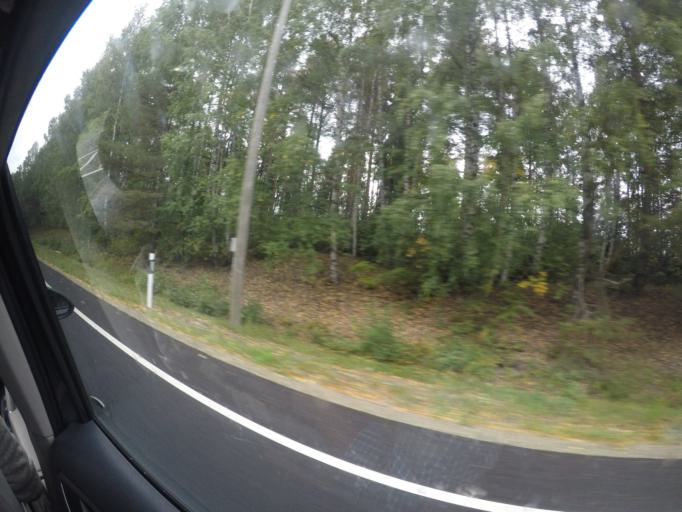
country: FI
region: Pirkanmaa
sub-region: Tampere
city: Kangasala
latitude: 61.4477
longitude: 24.1047
